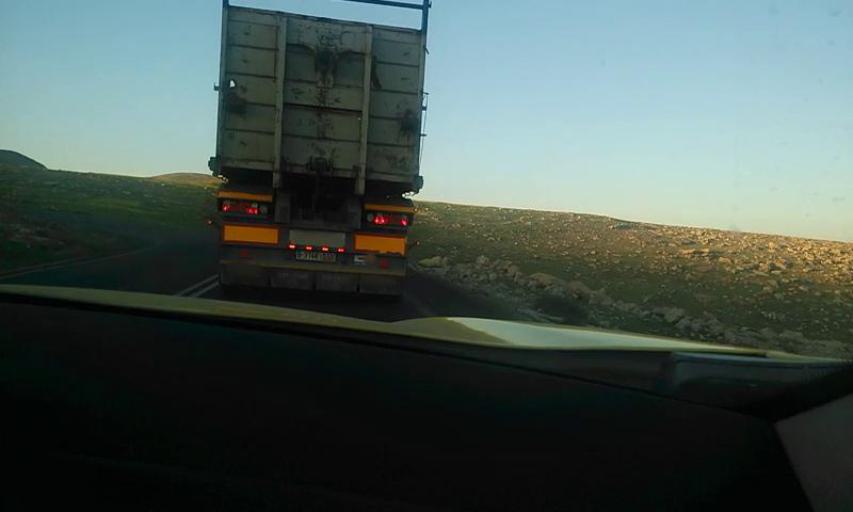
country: PS
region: West Bank
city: Rammun
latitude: 31.9167
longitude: 35.3459
